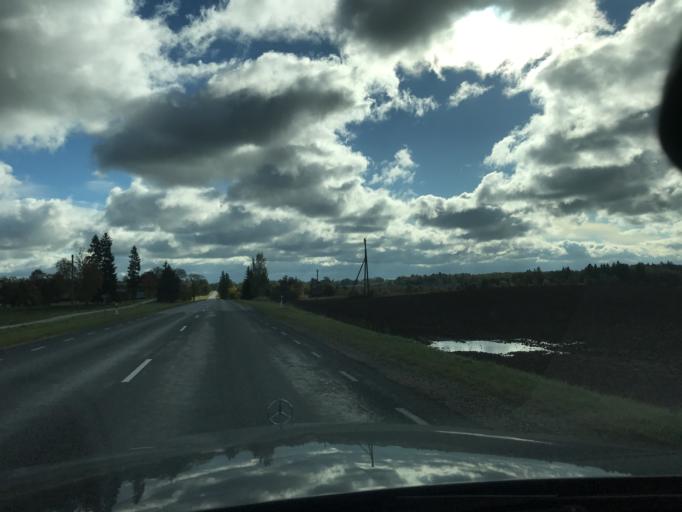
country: EE
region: Vorumaa
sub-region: Antsla vald
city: Vana-Antsla
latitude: 57.9506
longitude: 26.2872
